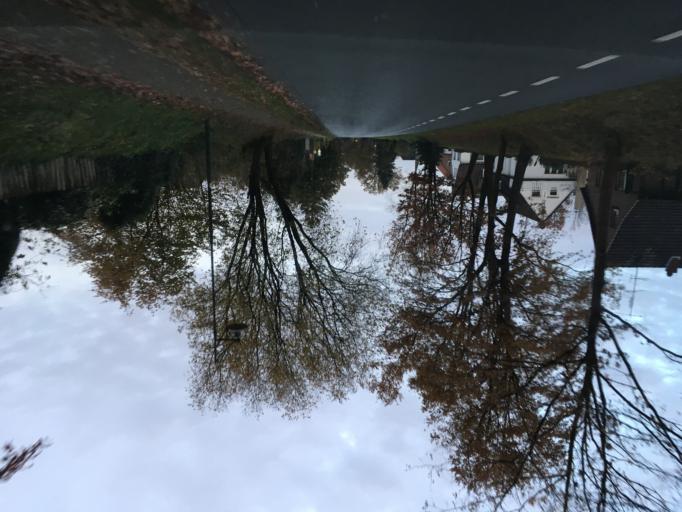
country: DE
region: Lower Saxony
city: Bispingen
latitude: 53.0933
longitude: 9.9984
